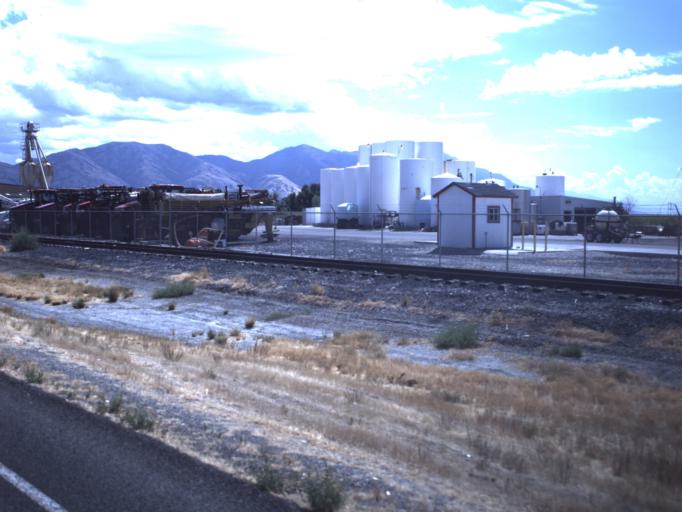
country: US
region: Utah
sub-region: Box Elder County
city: Honeyville
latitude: 41.5539
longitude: -112.1238
